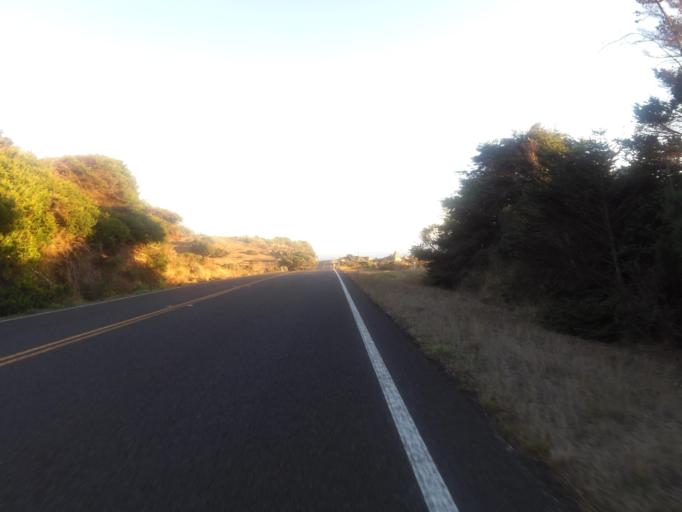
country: US
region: California
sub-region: Sonoma County
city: Sea Ranch
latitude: 38.6367
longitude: -123.3885
